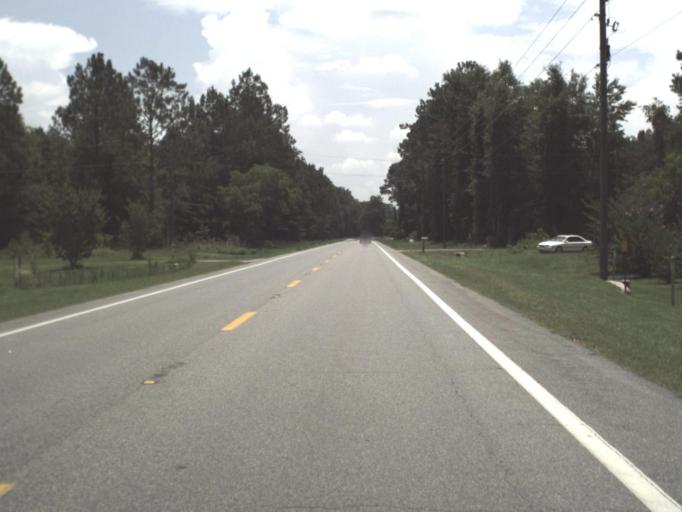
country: US
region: Florida
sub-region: Madison County
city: Madison
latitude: 30.4385
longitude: -83.3234
